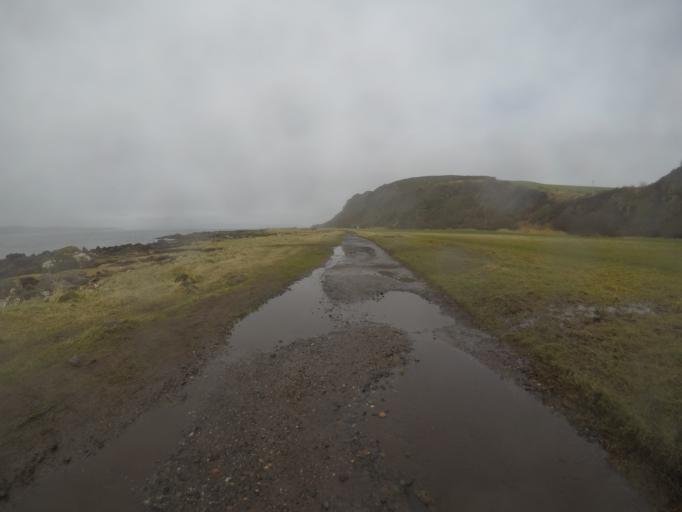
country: GB
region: Scotland
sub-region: North Ayrshire
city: Millport
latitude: 55.7027
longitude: -4.9043
